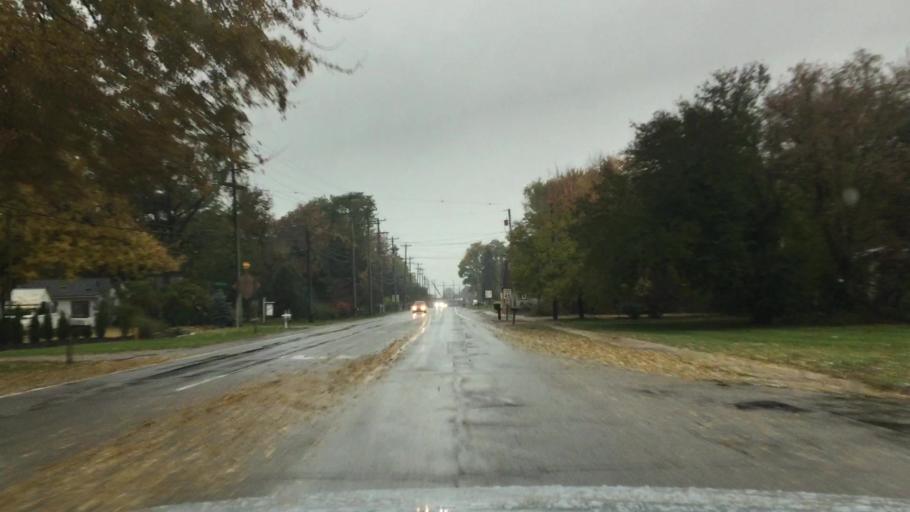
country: US
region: Michigan
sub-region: Saint Clair County
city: Algonac
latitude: 42.6170
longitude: -82.5515
